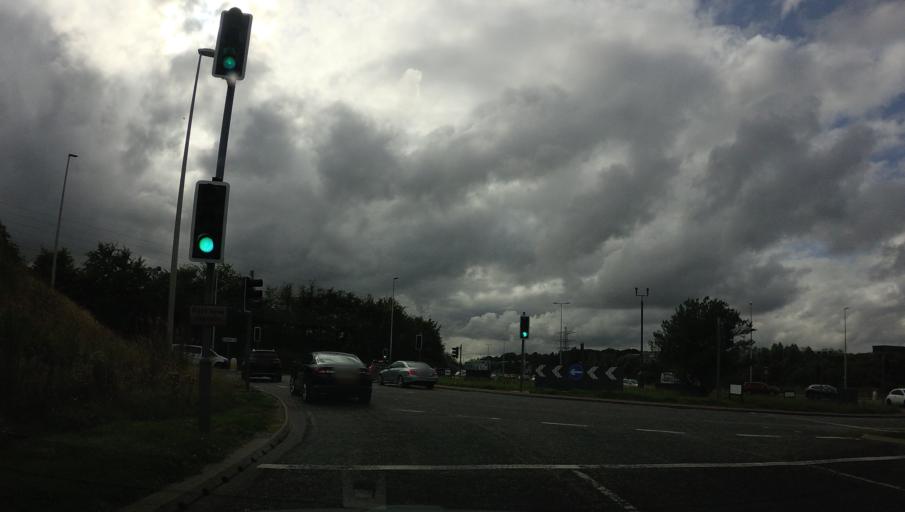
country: GB
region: Scotland
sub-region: Aberdeen City
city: Cults
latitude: 57.1466
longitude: -2.2192
